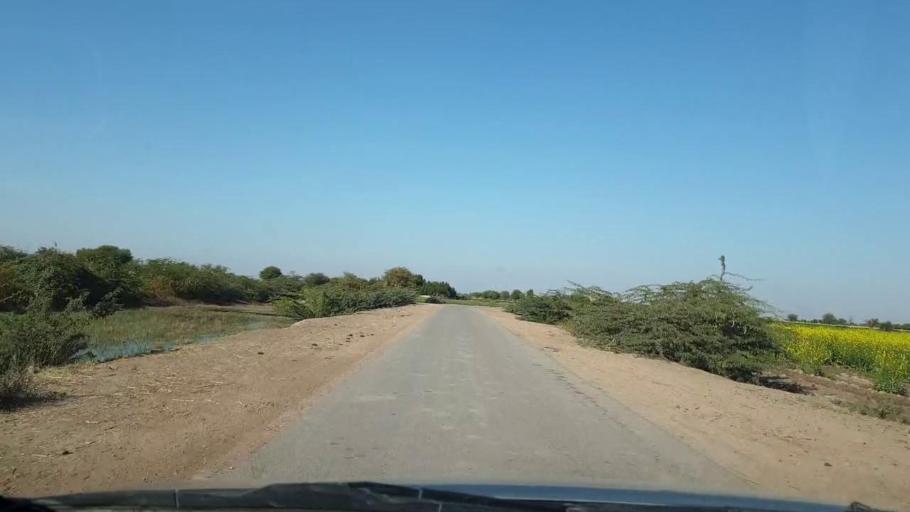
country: PK
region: Sindh
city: Jhol
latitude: 25.8254
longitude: 68.9482
